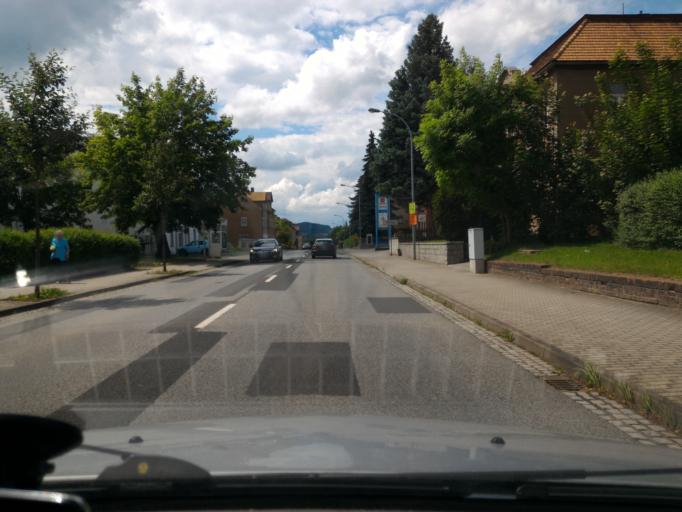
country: DE
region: Saxony
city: Olbersdorf
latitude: 50.8996
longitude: 14.7768
